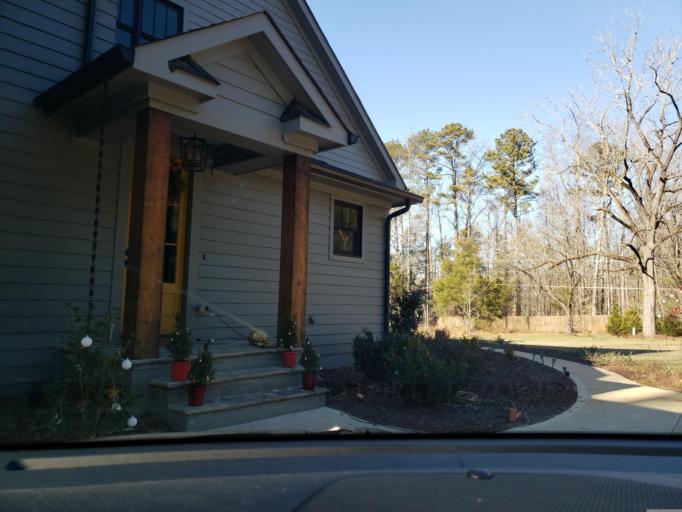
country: US
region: North Carolina
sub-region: Orange County
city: Chapel Hill
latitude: 35.9927
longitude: -79.0671
